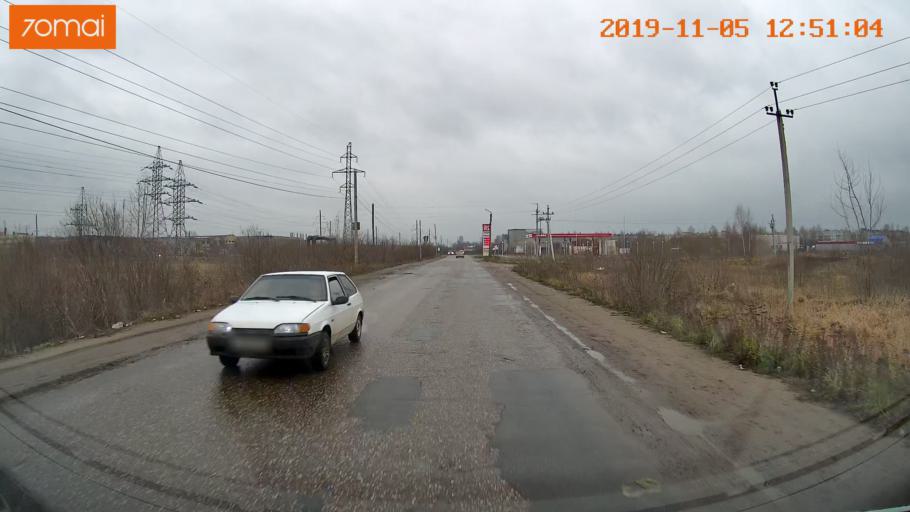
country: RU
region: Ivanovo
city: Kokhma
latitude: 56.9446
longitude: 41.1127
